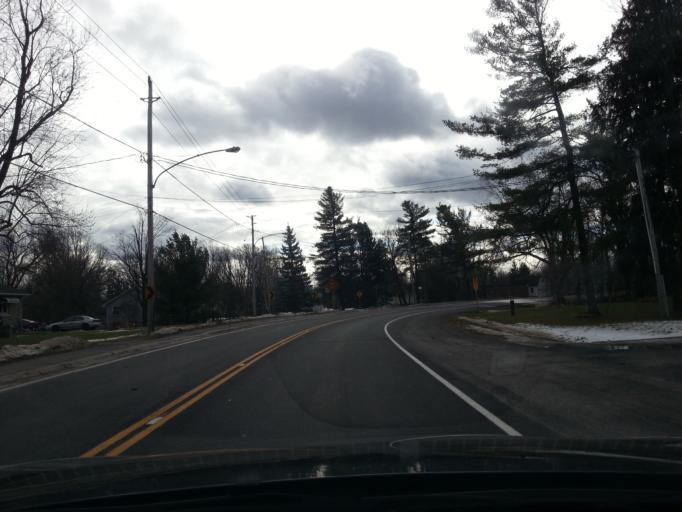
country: CA
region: Ontario
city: Bells Corners
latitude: 45.1356
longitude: -75.7152
